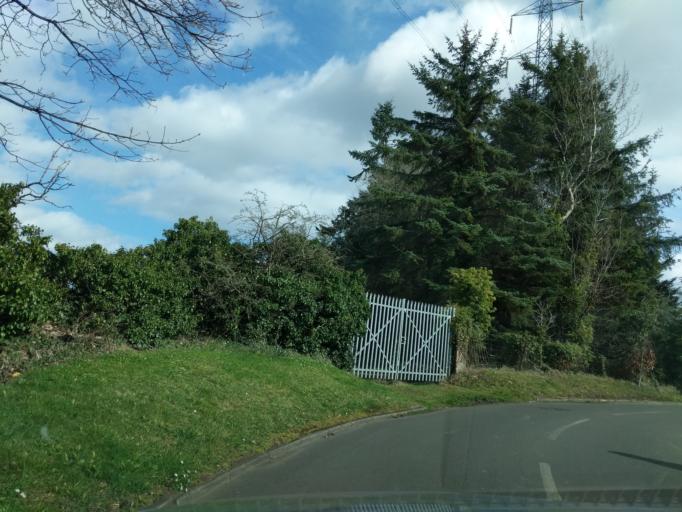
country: GB
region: Scotland
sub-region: Edinburgh
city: Currie
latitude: 55.9035
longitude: -3.2982
